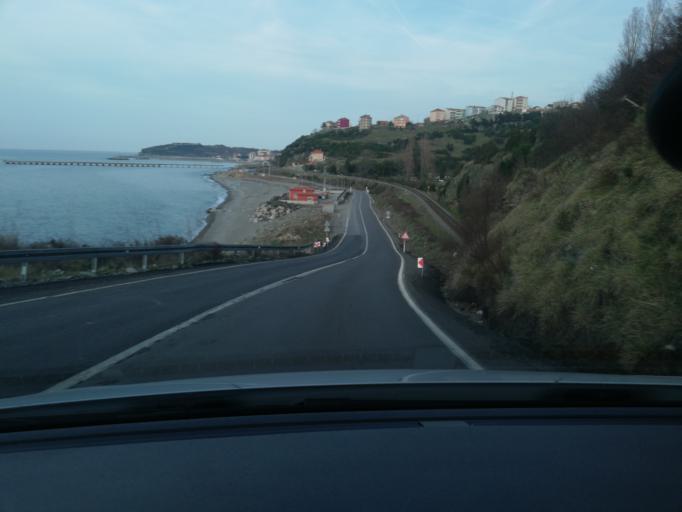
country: TR
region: Zonguldak
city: Tieum
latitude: 41.5536
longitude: 32.0081
